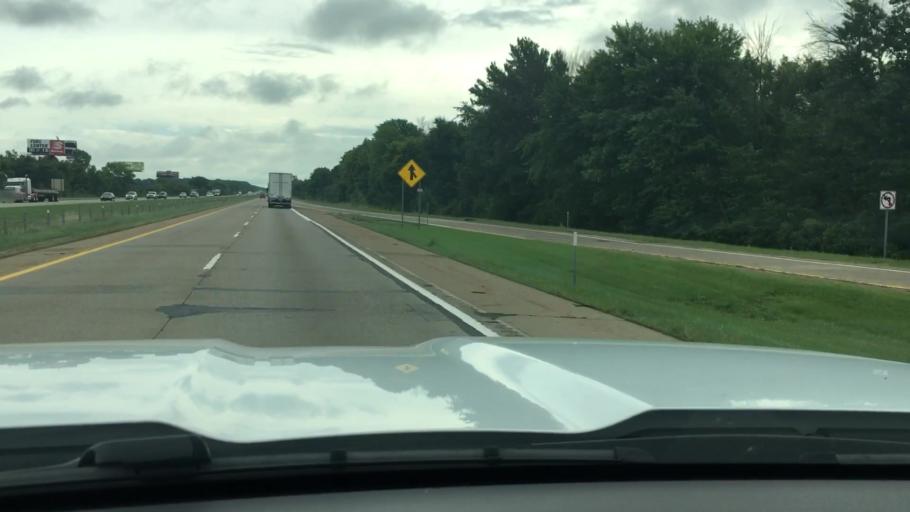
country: US
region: Michigan
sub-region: Ionia County
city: Ionia
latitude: 42.8787
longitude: -85.0325
